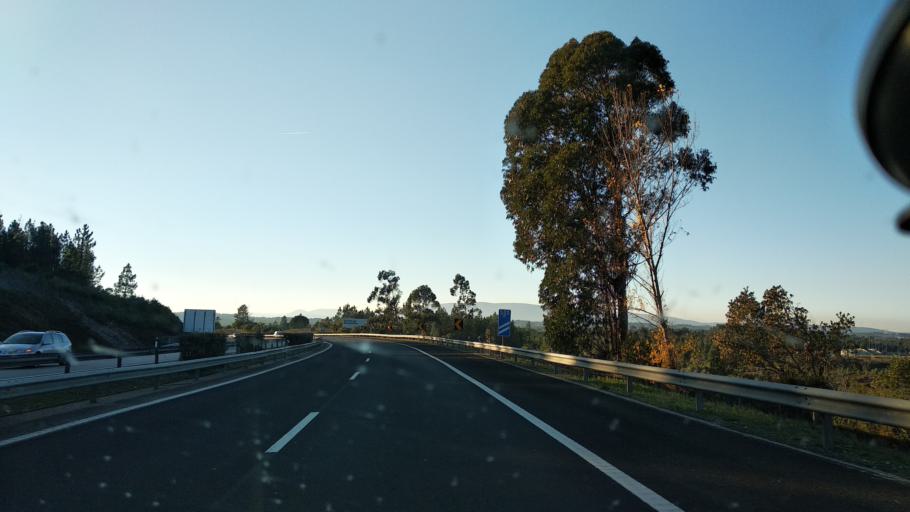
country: PT
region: Santarem
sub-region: Entroncamento
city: Entroncamento
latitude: 39.4908
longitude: -8.4371
